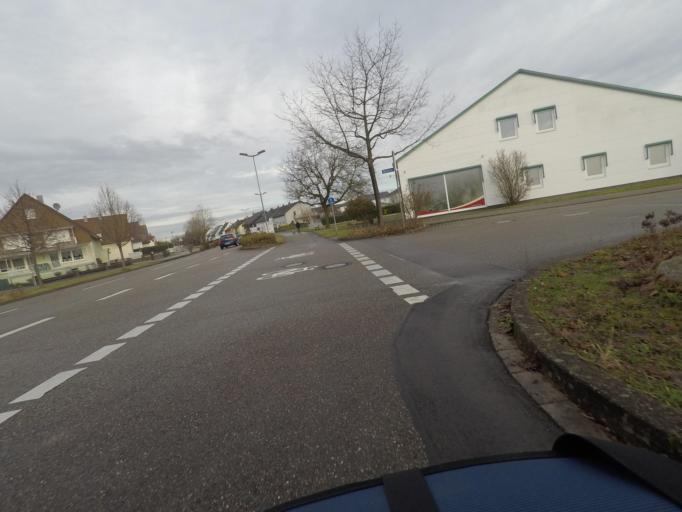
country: DE
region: Baden-Wuerttemberg
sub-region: Karlsruhe Region
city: Steinmauern
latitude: 48.8941
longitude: 8.1958
